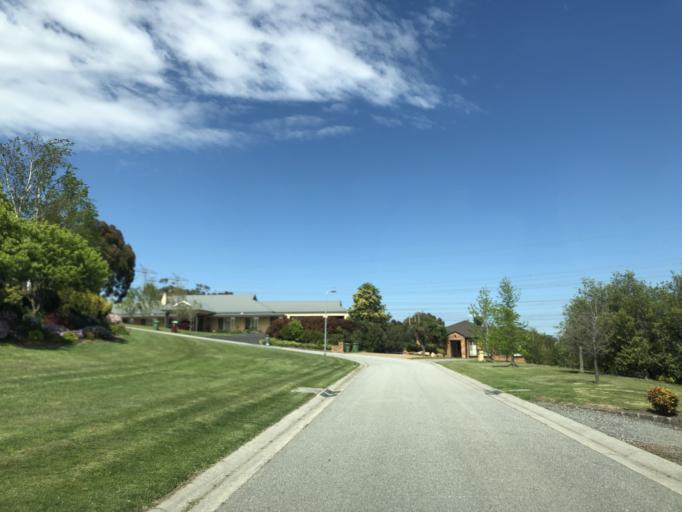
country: AU
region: Victoria
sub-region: Casey
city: Endeavour Hills
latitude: -37.9699
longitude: 145.2870
